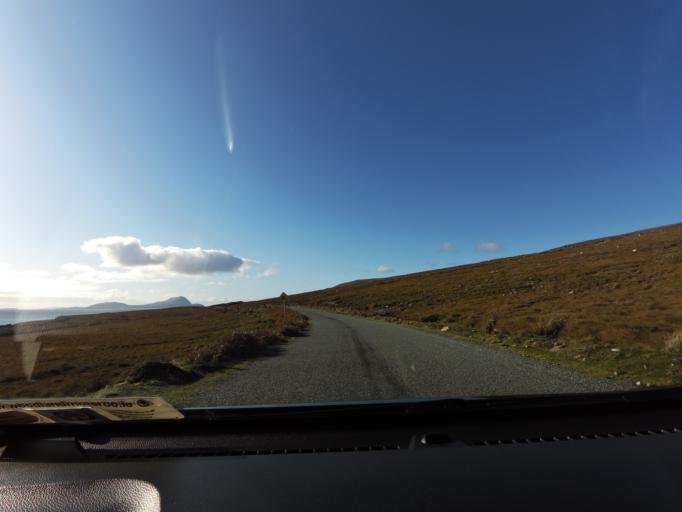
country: IE
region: Connaught
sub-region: Maigh Eo
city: Westport
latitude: 53.8762
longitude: -9.8282
